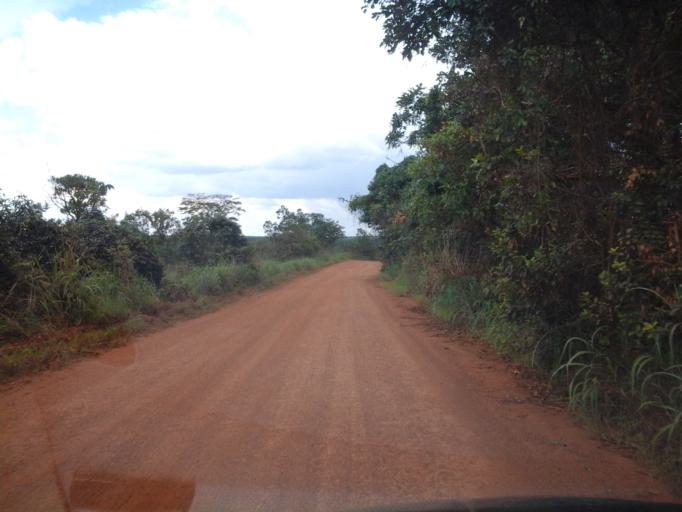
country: BR
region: Goias
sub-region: Abadiania
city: Abadiania
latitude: -16.0009
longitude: -48.5534
